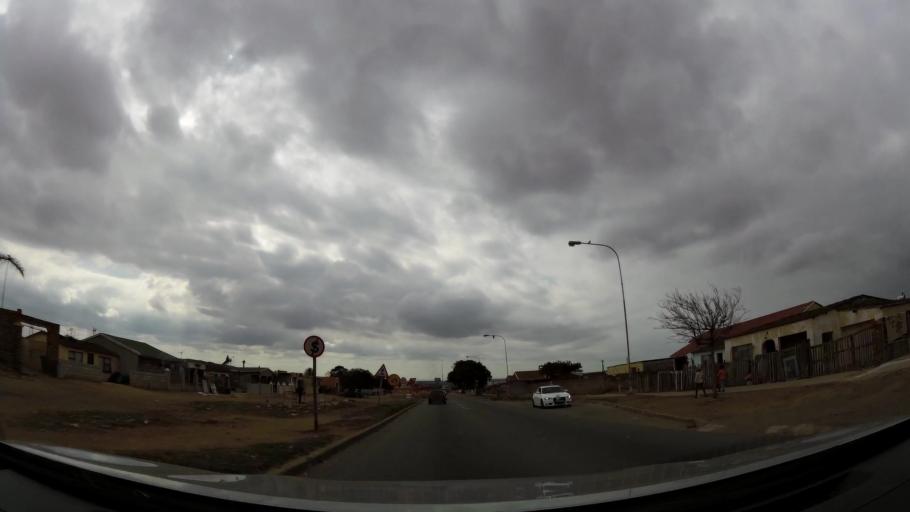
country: ZA
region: Eastern Cape
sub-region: Nelson Mandela Bay Metropolitan Municipality
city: Port Elizabeth
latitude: -33.8731
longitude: 25.5638
